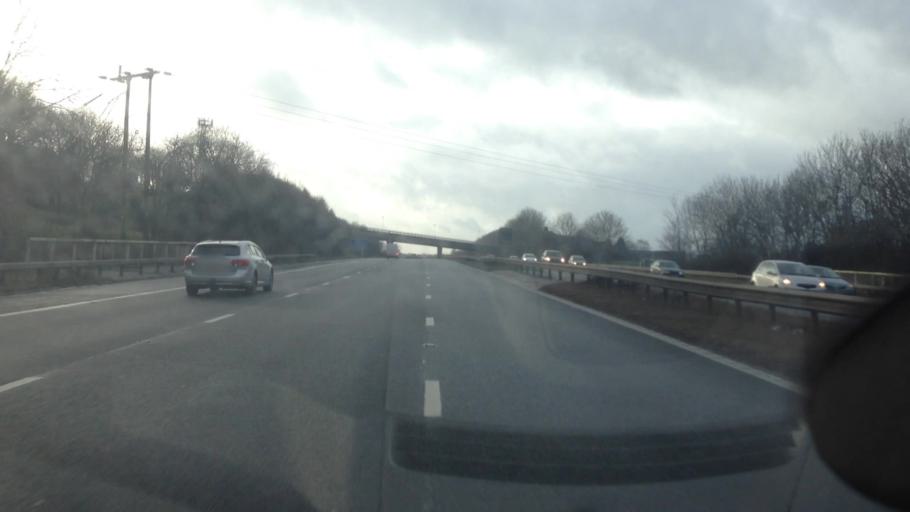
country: GB
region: England
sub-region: City and Borough of Wakefield
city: Crigglestone
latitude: 53.6429
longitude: -1.5337
